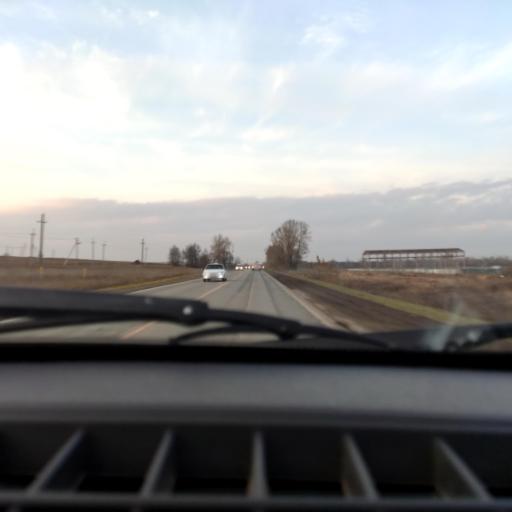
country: RU
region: Bashkortostan
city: Avdon
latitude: 54.7229
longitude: 55.8076
